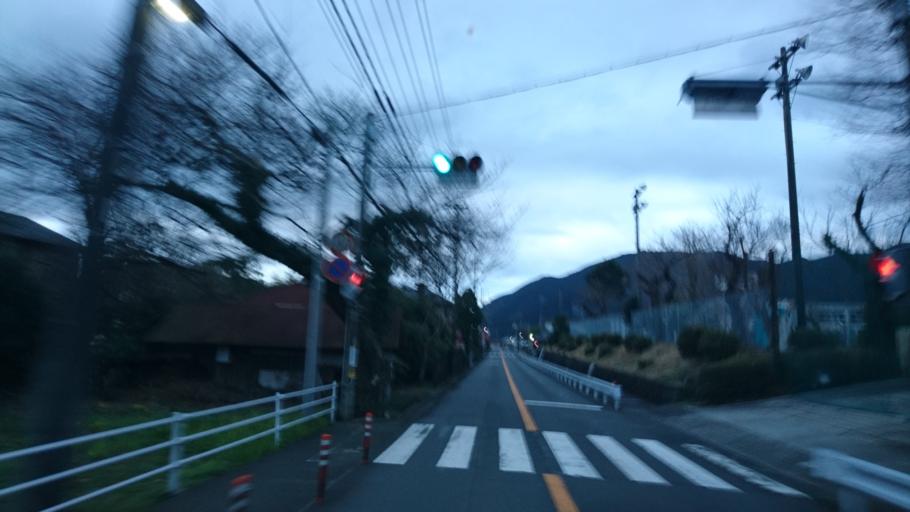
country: JP
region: Shizuoka
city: Fujinomiya
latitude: 35.3136
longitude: 138.5792
